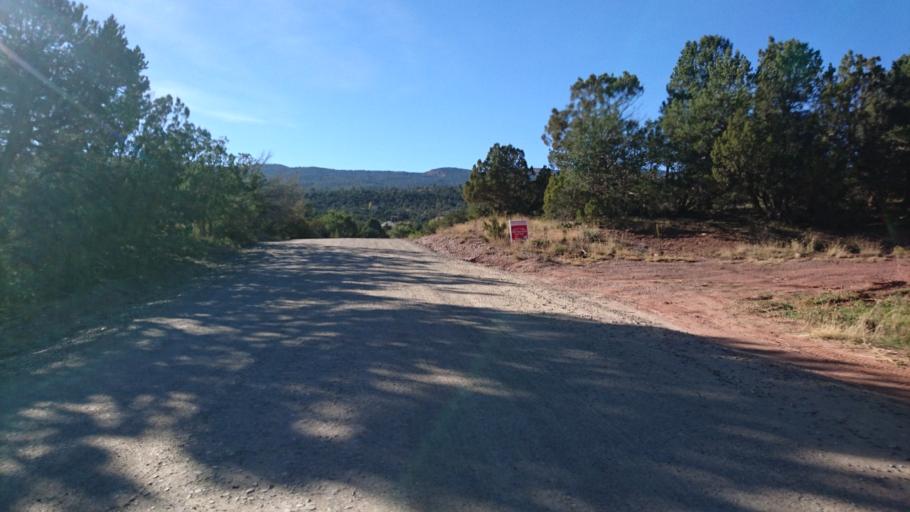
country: US
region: New Mexico
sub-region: Bernalillo County
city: Sandia Knolls
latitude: 35.1406
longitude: -106.3643
